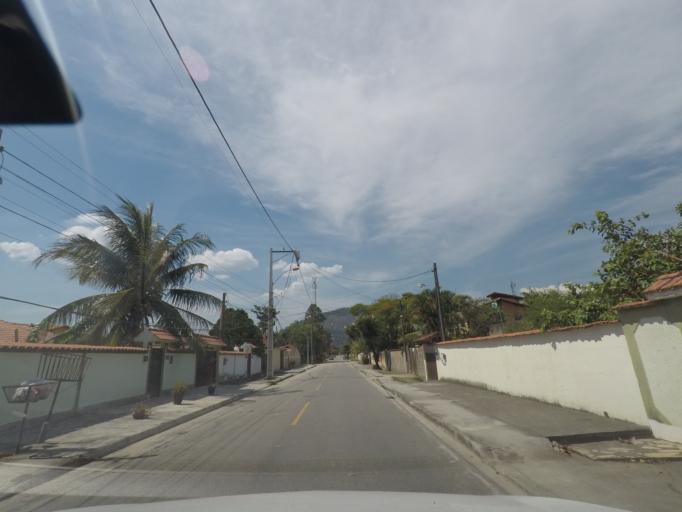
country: BR
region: Rio de Janeiro
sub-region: Marica
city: Marica
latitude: -22.9628
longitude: -42.9640
